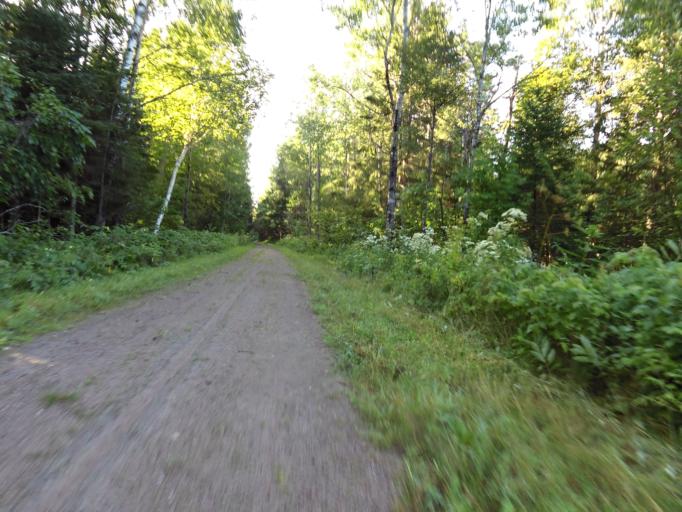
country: CA
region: Quebec
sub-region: Outaouais
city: Maniwaki
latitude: 46.2855
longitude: -76.0240
